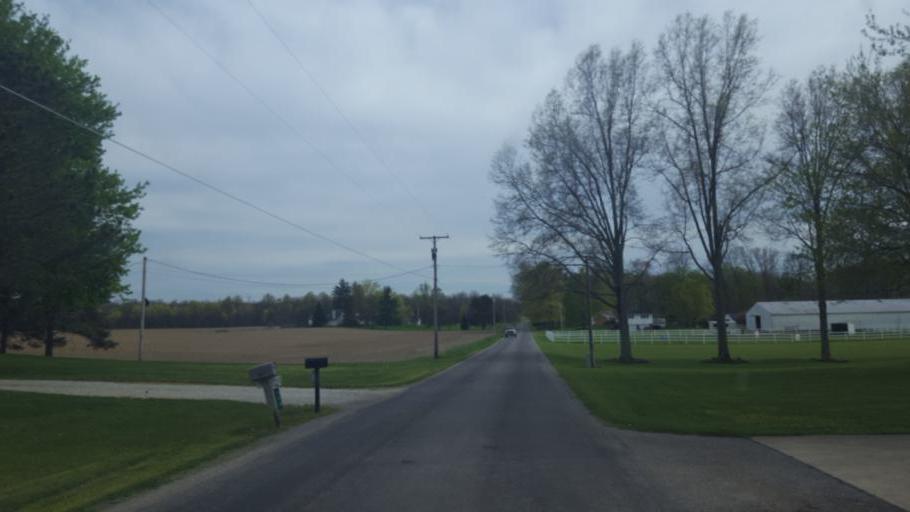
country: US
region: Ohio
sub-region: Crawford County
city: Crestline
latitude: 40.7448
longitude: -82.7220
